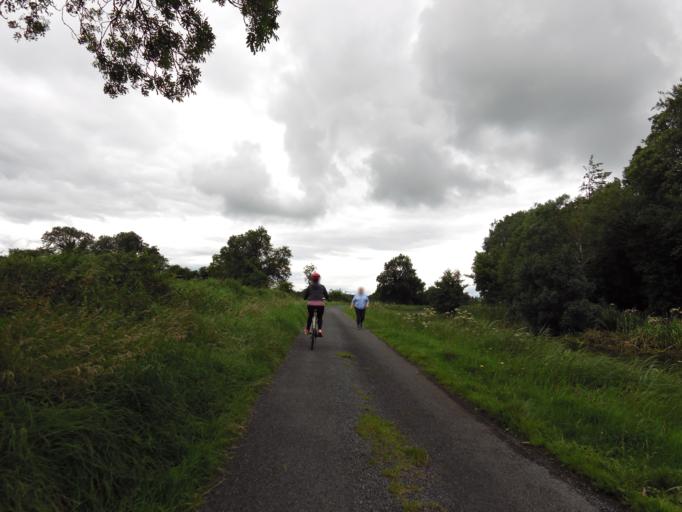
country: IE
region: Leinster
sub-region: An Iarmhi
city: An Muileann gCearr
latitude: 53.5382
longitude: -7.4743
